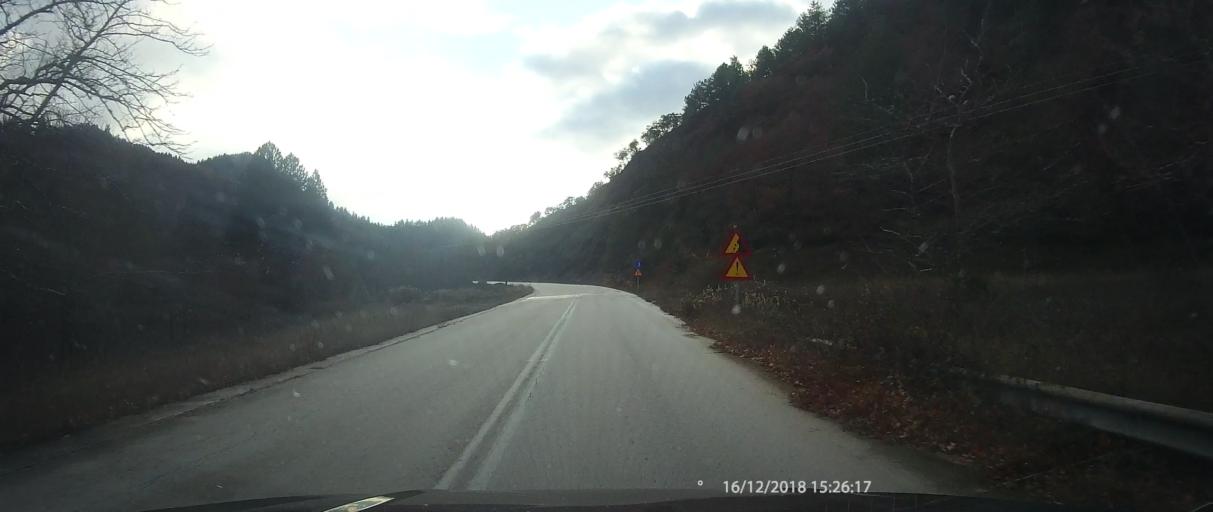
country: GR
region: Epirus
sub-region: Nomos Ioanninon
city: Konitsa
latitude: 40.1195
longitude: 20.7812
